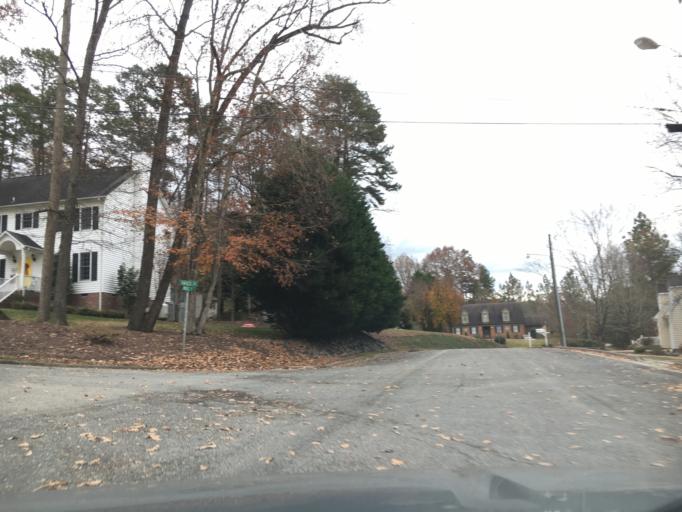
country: US
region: Virginia
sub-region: Halifax County
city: South Boston
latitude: 36.7261
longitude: -78.9130
